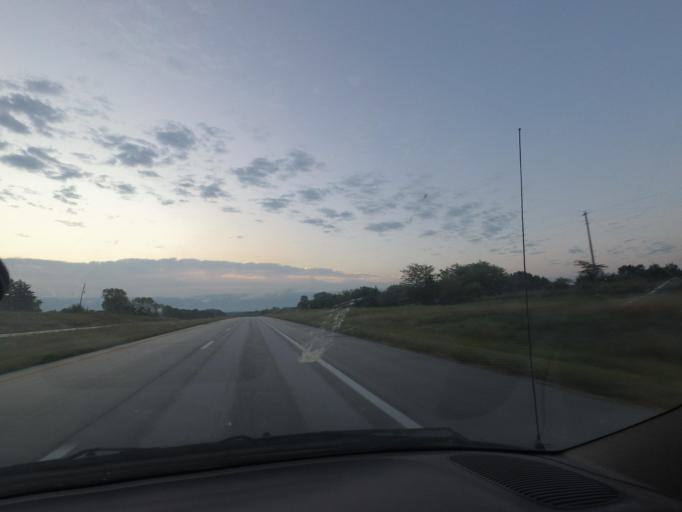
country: US
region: Missouri
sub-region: Macon County
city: Macon
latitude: 39.7532
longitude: -92.5349
